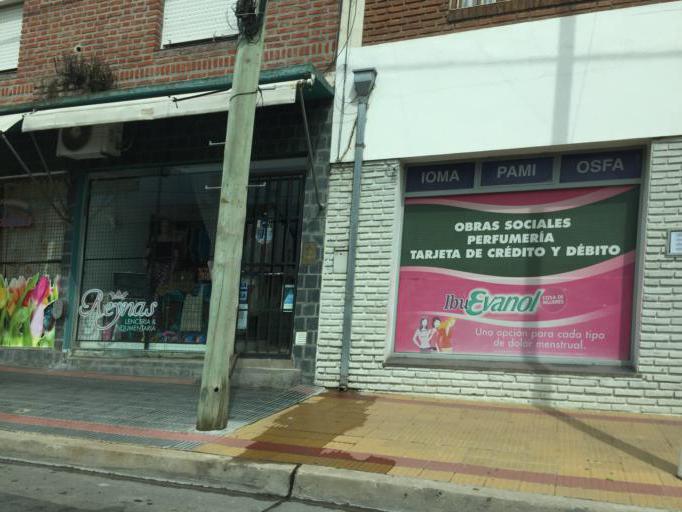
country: AR
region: Buenos Aires
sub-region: Partido de Tandil
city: Tandil
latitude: -37.3256
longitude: -59.1128
